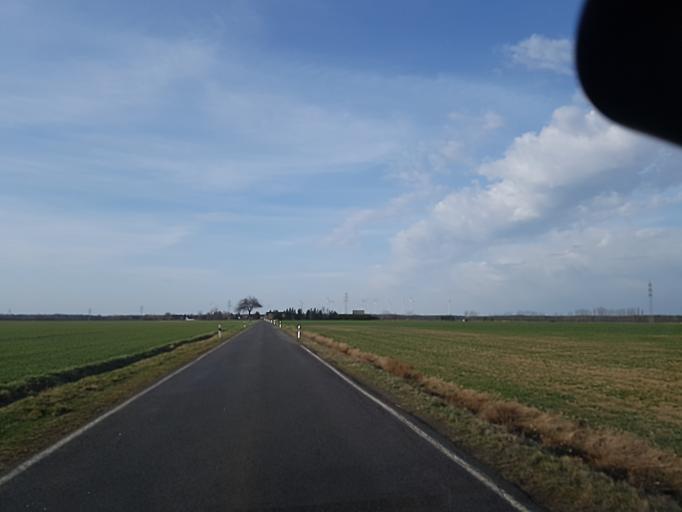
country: DE
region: Brandenburg
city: Falkenberg
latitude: 51.5376
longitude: 13.2951
